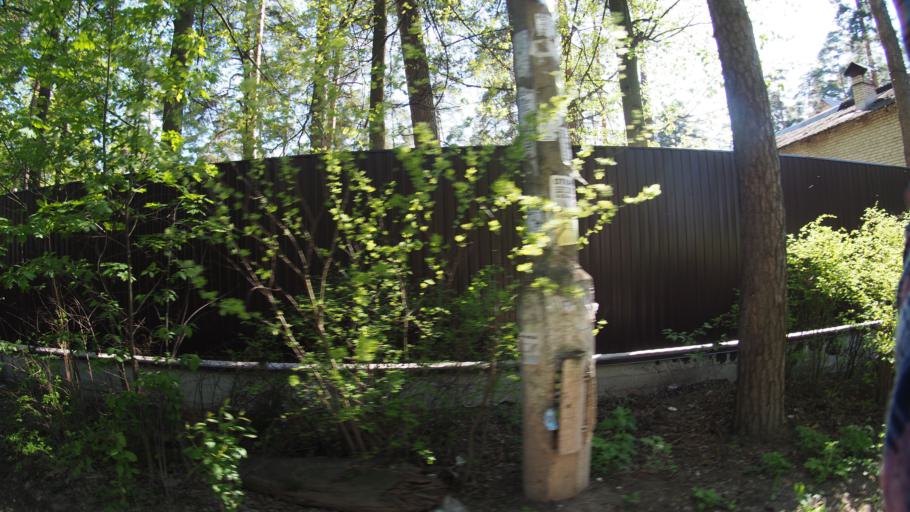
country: RU
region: Moskovskaya
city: Kratovo
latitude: 55.5780
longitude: 38.1803
